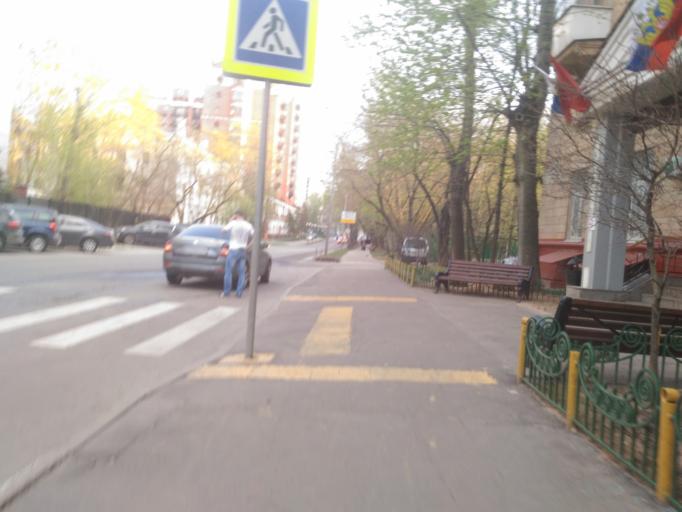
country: RU
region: Moskovskaya
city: Khoroshevo-Mnevniki
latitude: 55.7942
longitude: 37.4835
